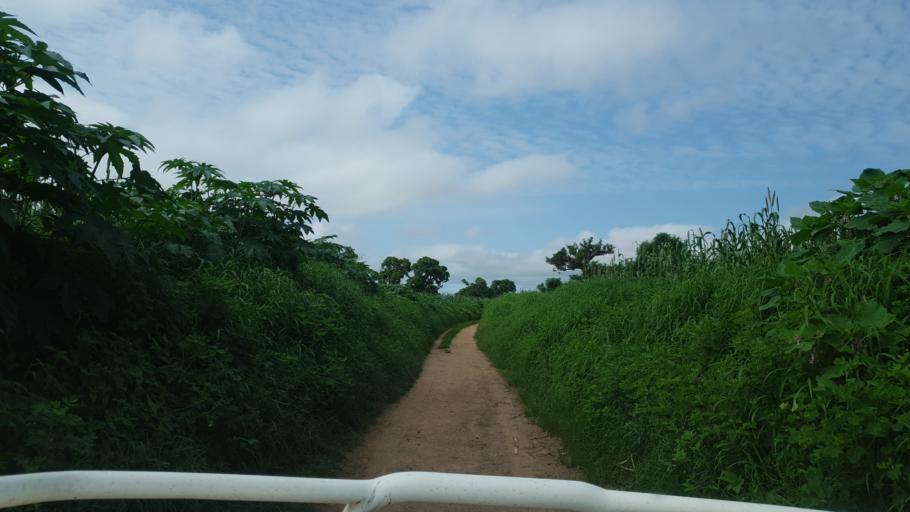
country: ML
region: Segou
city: Baroueli
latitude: 13.4843
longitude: -6.8962
